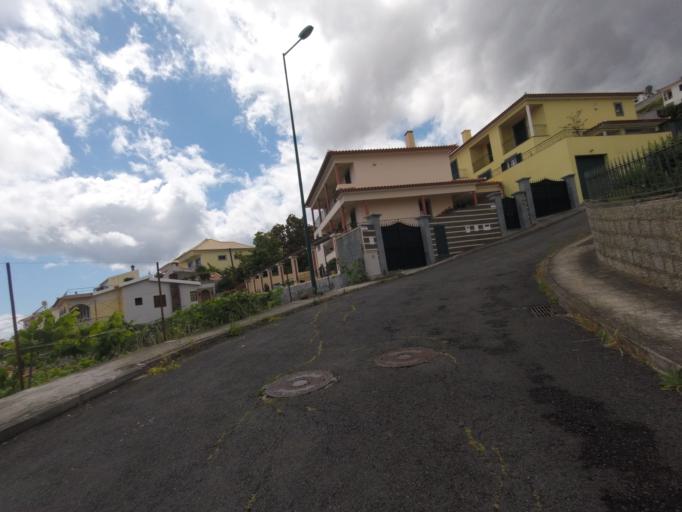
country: PT
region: Madeira
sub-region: Funchal
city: Nossa Senhora do Monte
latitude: 32.6673
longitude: -16.9095
